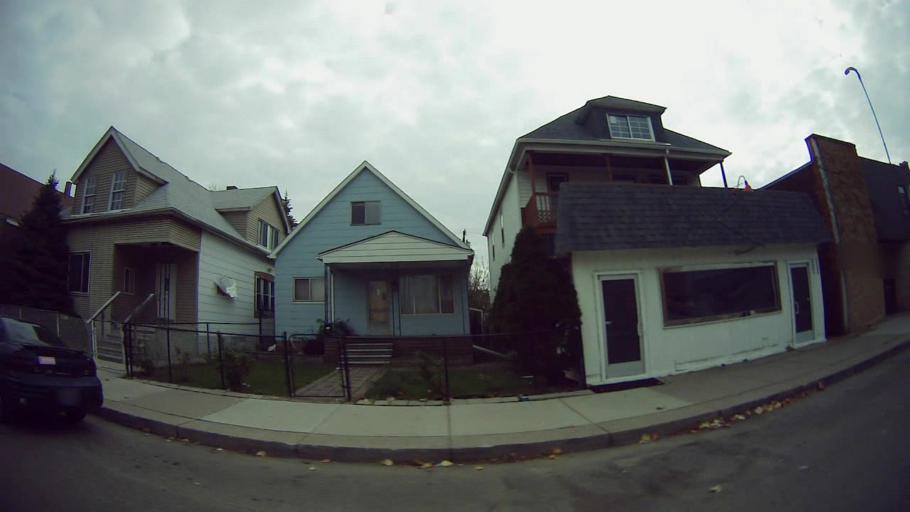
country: US
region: Michigan
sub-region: Wayne County
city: Hamtramck
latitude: 42.4002
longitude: -83.0586
